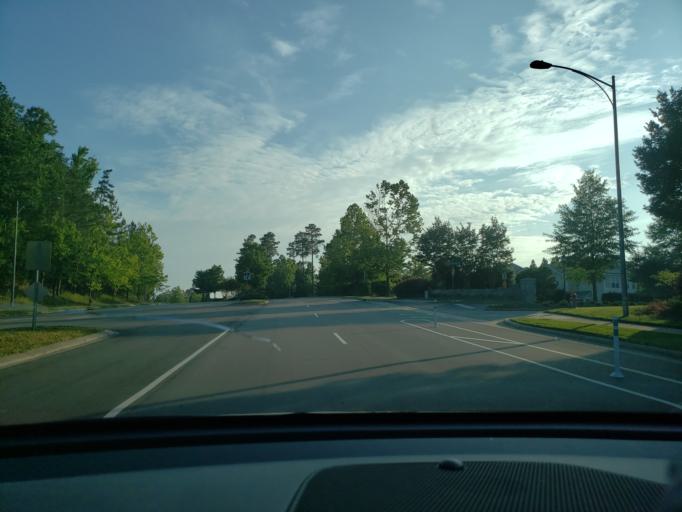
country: US
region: North Carolina
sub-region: Durham County
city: Durham
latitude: 35.9467
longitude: -78.9261
